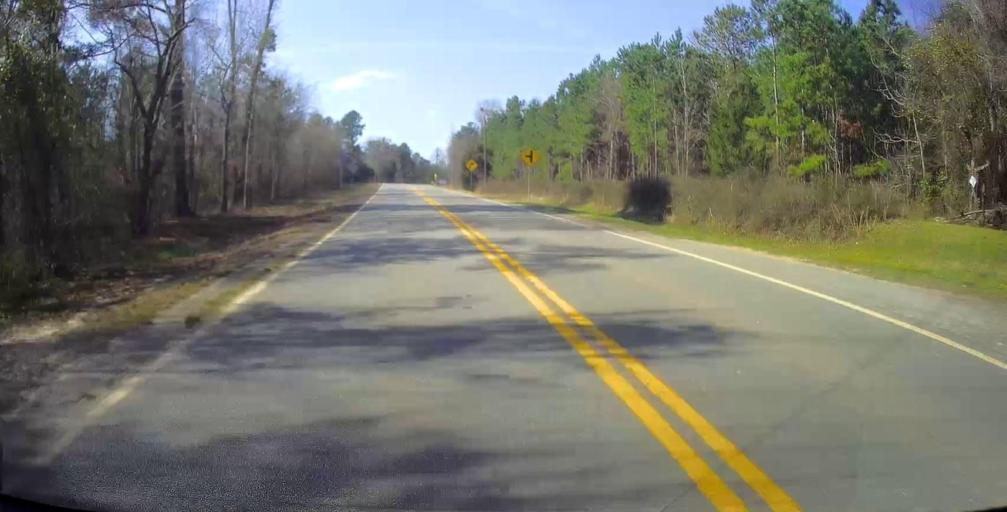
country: US
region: Georgia
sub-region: Wilkinson County
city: Gordon
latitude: 32.8544
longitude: -83.3460
